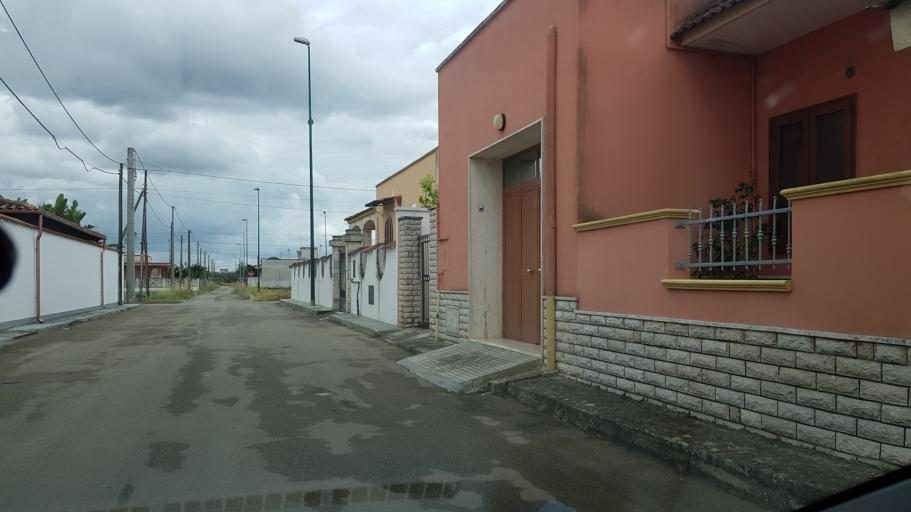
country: IT
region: Apulia
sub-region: Provincia di Brindisi
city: Torchiarolo
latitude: 40.4818
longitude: 18.0477
